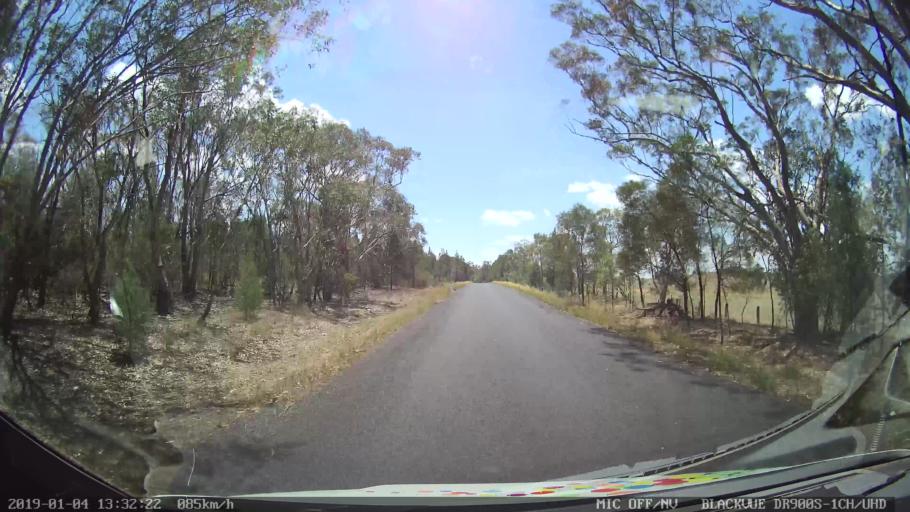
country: AU
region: New South Wales
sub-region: Dubbo Municipality
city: Eulomogo
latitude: -32.6104
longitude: 148.5483
